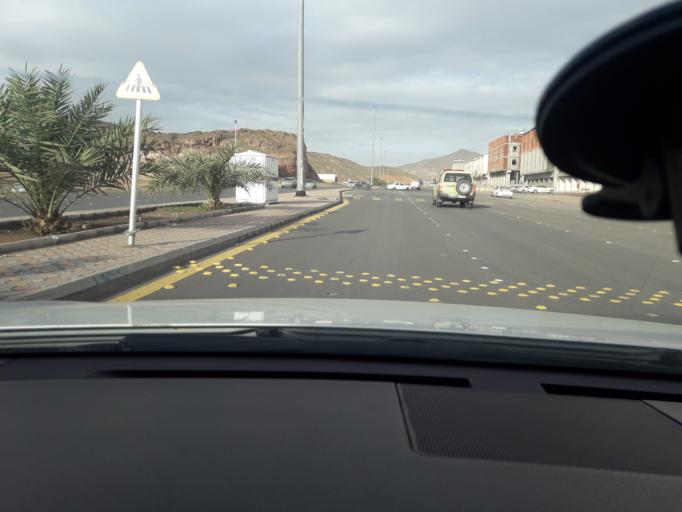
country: SA
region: Al Madinah al Munawwarah
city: Sultanah
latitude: 24.4655
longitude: 39.5089
